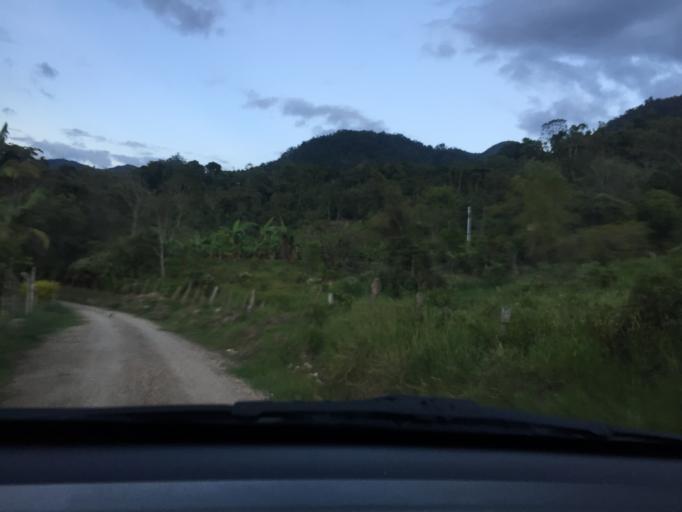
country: CO
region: Cundinamarca
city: Zipacon
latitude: 4.7057
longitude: -74.4094
